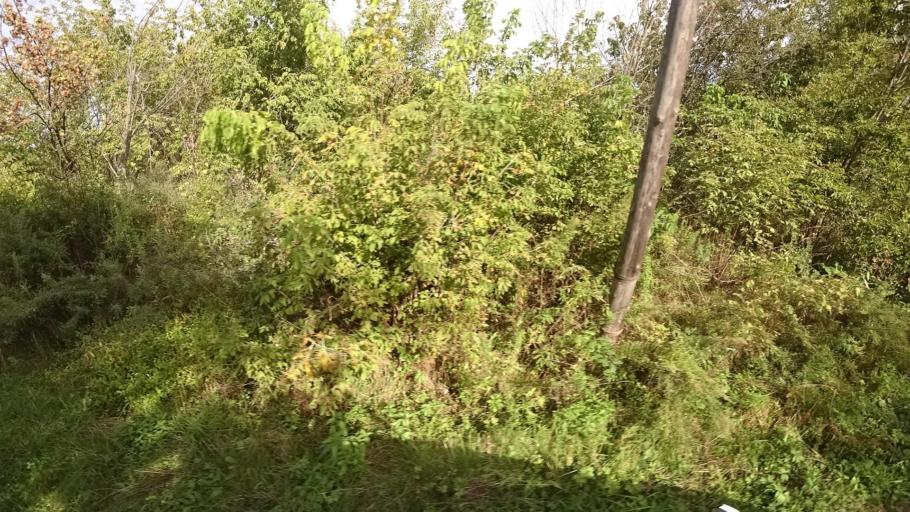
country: RU
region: Primorskiy
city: Dostoyevka
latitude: 44.3270
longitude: 133.4847
